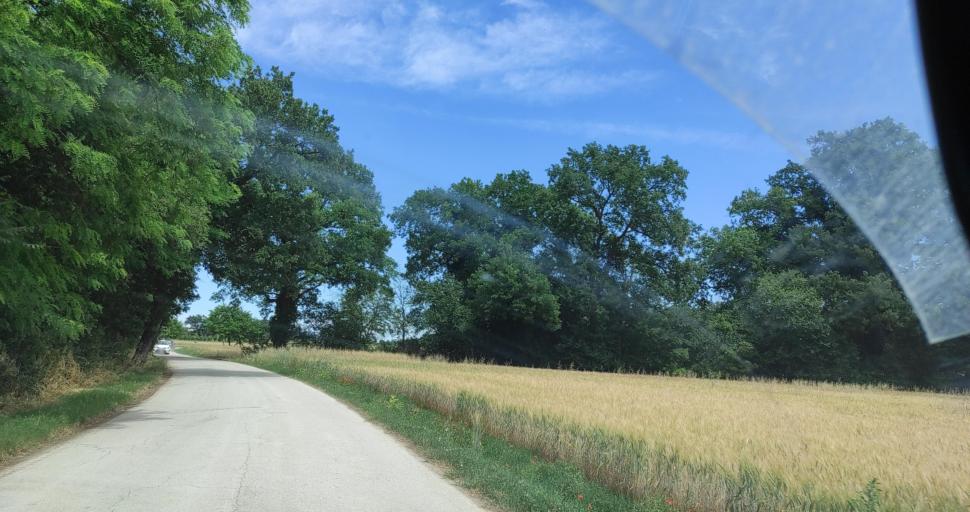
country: IT
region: The Marches
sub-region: Provincia di Macerata
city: Urbisaglia
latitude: 43.2099
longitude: 13.3998
